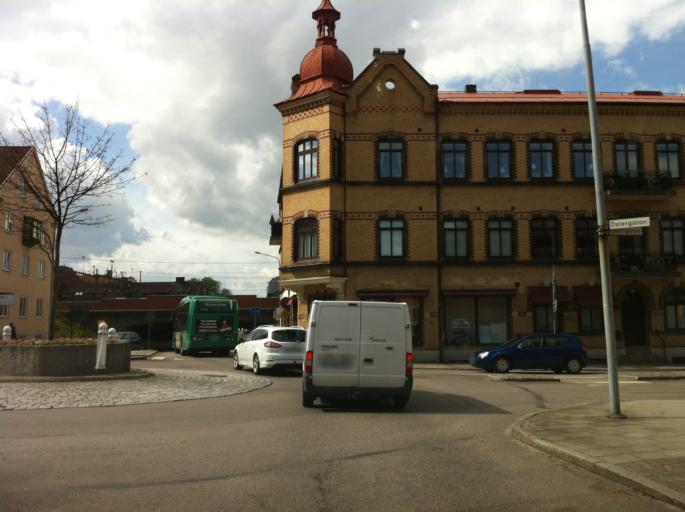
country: SE
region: Skane
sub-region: Eslovs Kommun
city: Eslov
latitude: 55.8392
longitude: 13.3079
